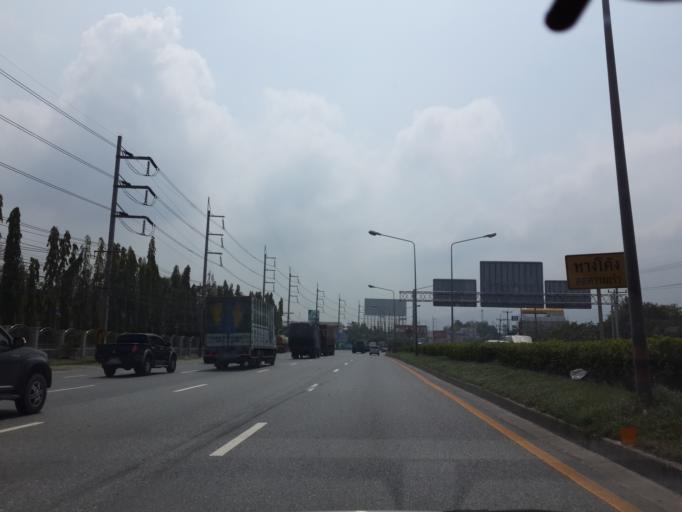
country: TH
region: Chon Buri
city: Chon Buri
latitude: 13.3830
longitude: 101.0184
